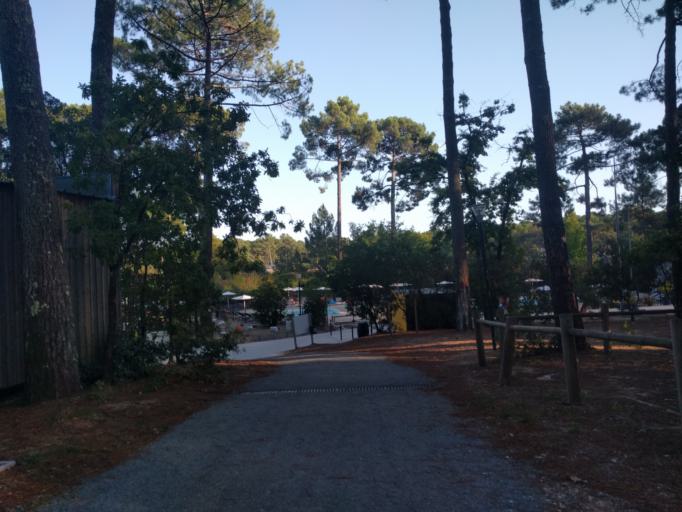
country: FR
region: Aquitaine
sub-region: Departement de la Gironde
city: Ares
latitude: 44.7529
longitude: -1.1875
